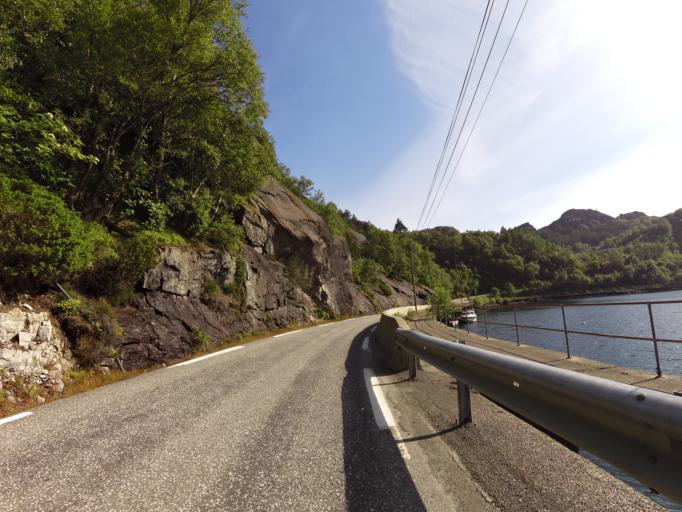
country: NO
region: Rogaland
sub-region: Sokndal
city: Hauge i Dalane
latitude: 58.3193
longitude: 6.3485
